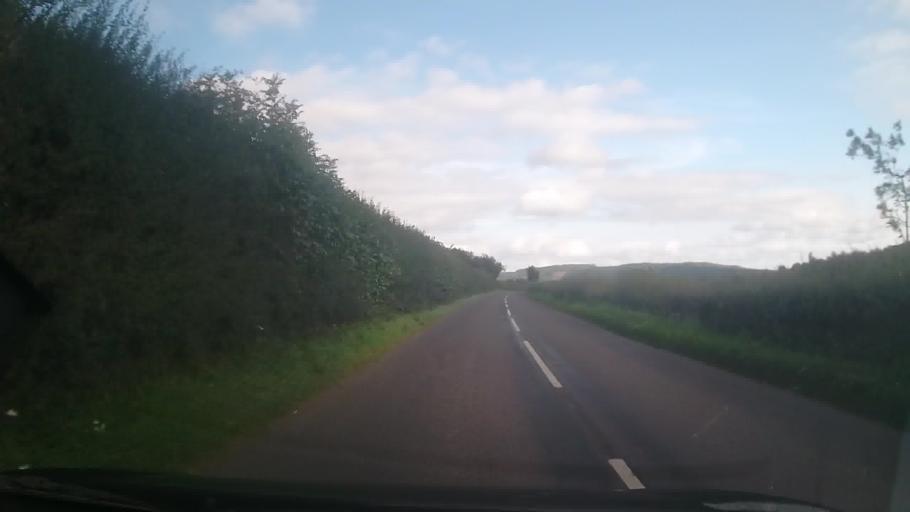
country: GB
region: England
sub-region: Shropshire
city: Bishop's Castle
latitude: 52.4684
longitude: -2.9735
